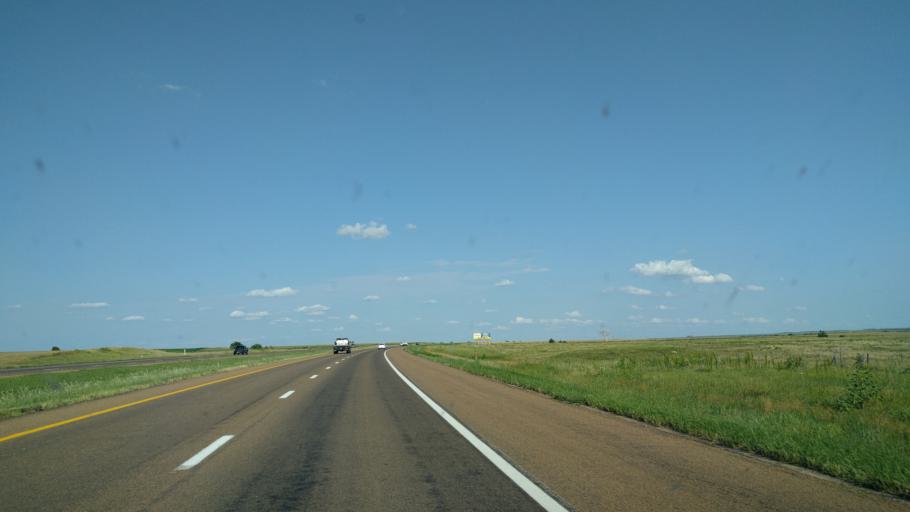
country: US
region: Kansas
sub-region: Ellis County
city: Ellis
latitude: 38.9497
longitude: -99.5269
